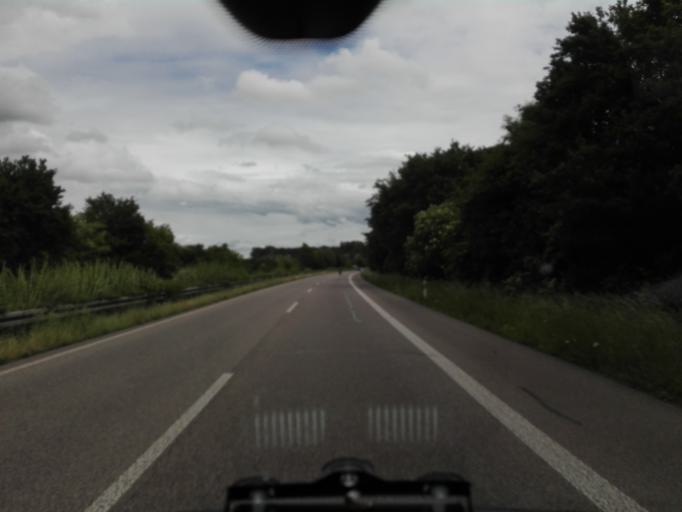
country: DE
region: Baden-Wuerttemberg
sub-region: Karlsruhe Region
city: Eggenstein-Leopoldshafen
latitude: 49.0548
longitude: 8.3688
